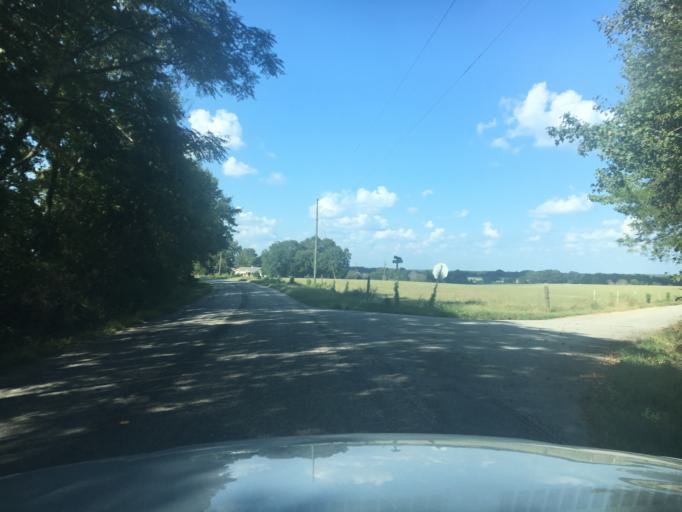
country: US
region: South Carolina
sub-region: Greenwood County
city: Ware Shoals
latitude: 34.4722
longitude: -82.2398
